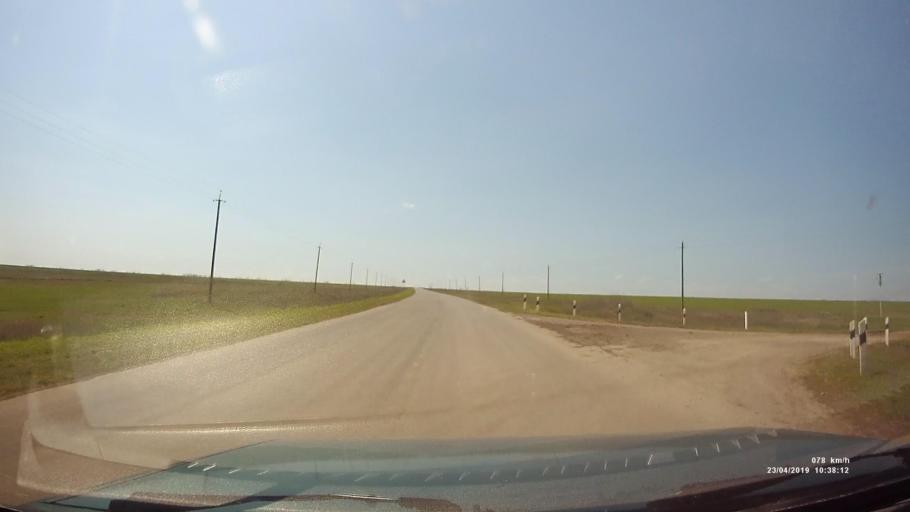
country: RU
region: Kalmykiya
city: Yashalta
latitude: 46.5349
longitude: 42.6389
